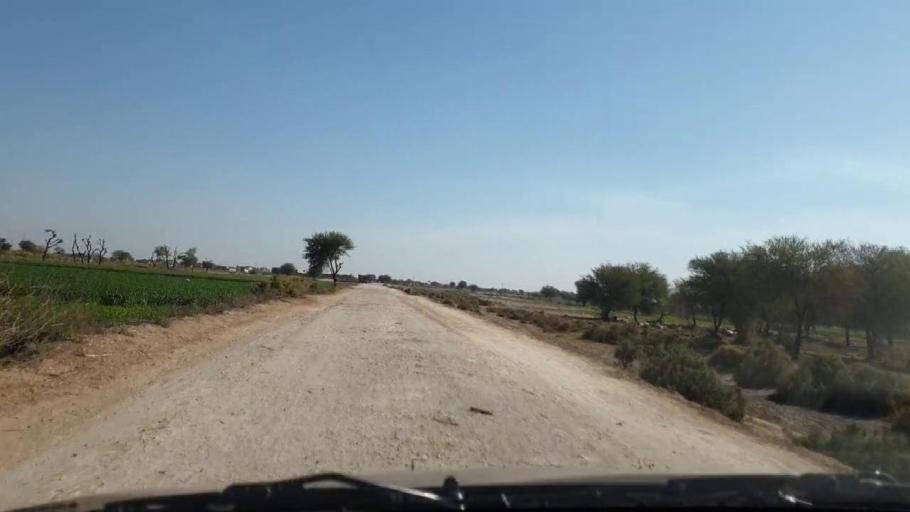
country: PK
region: Sindh
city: Sinjhoro
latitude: 26.1290
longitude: 68.8202
